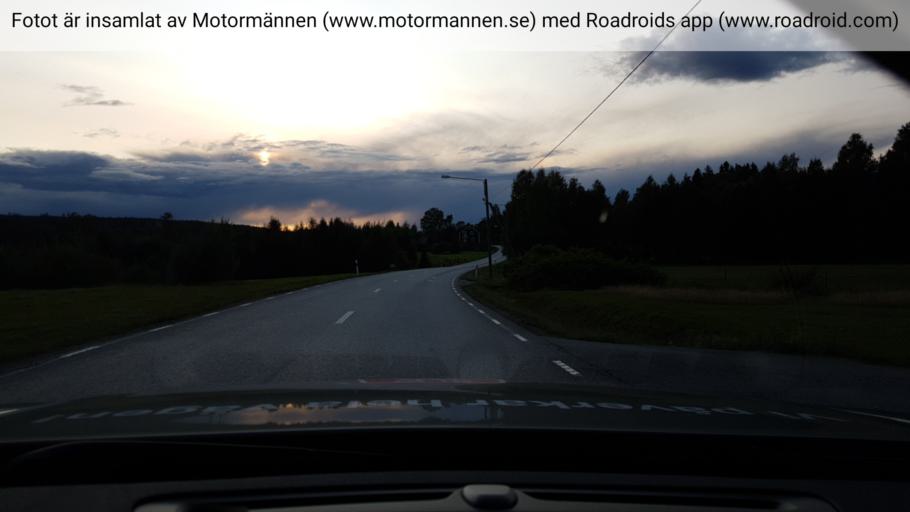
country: SE
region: OErebro
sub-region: Ljusnarsbergs Kommun
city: Kopparberg
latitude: 59.7783
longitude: 14.7917
